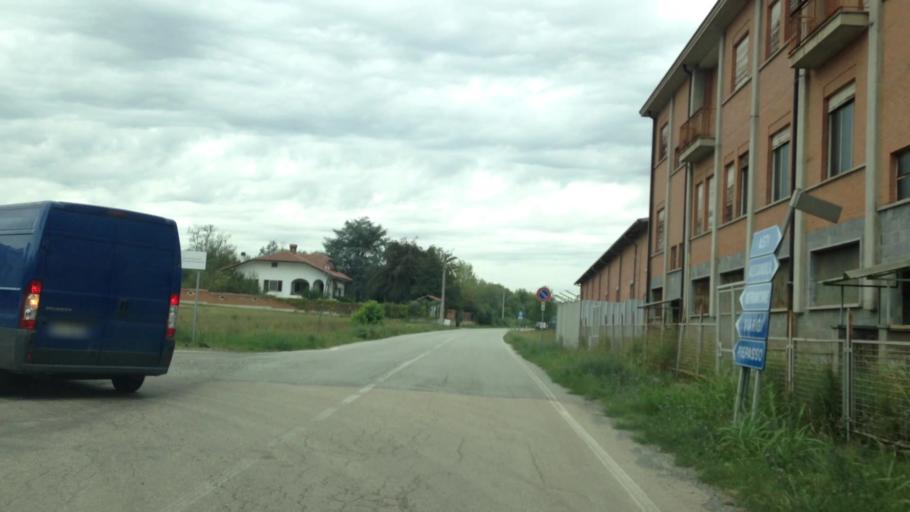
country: IT
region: Piedmont
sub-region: Provincia di Alessandria
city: Quattordio
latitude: 44.9030
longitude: 8.4046
